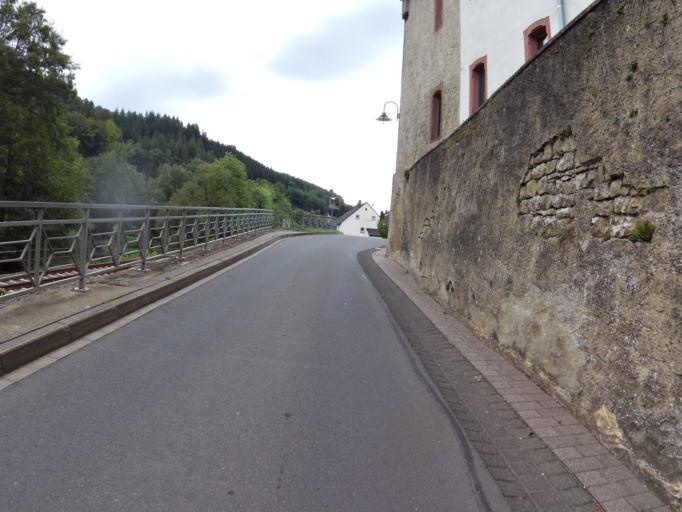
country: DE
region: Rheinland-Pfalz
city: Sankt Thomas
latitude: 50.0688
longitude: 6.6008
